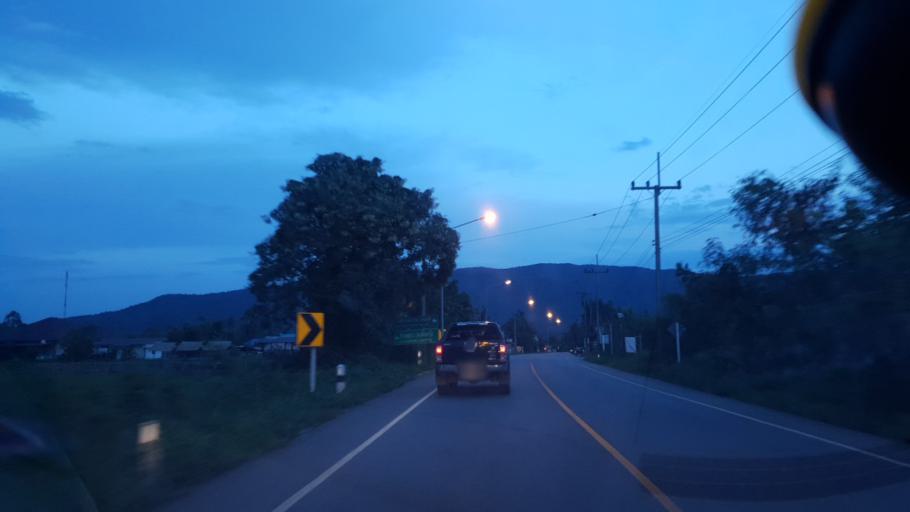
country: TH
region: Chiang Rai
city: Wiang Chiang Rung
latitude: 19.9646
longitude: 100.0043
